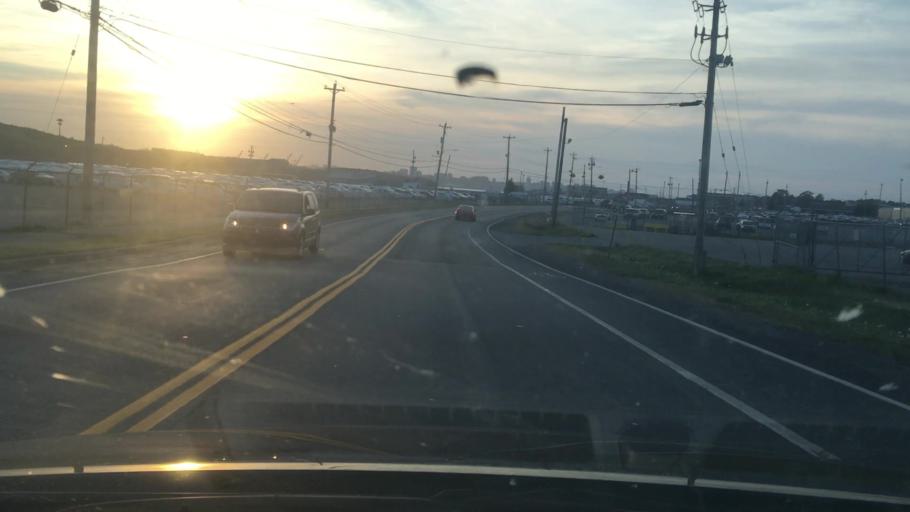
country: CA
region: Nova Scotia
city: Cole Harbour
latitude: 44.6202
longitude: -63.5050
